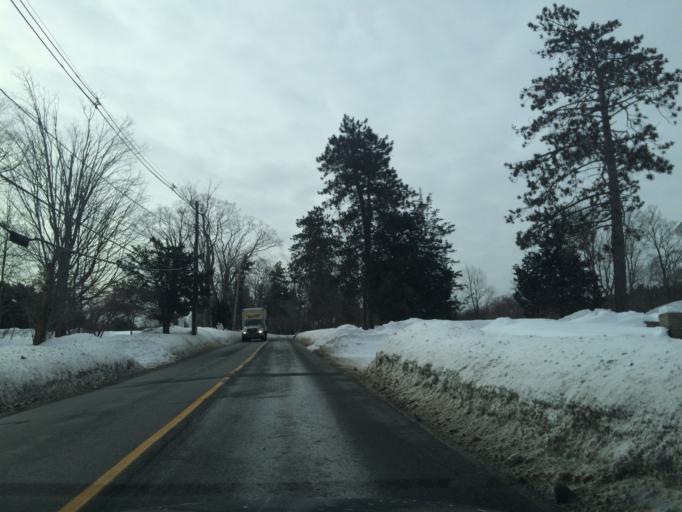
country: US
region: Massachusetts
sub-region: Middlesex County
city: Weston
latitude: 42.3339
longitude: -71.3068
